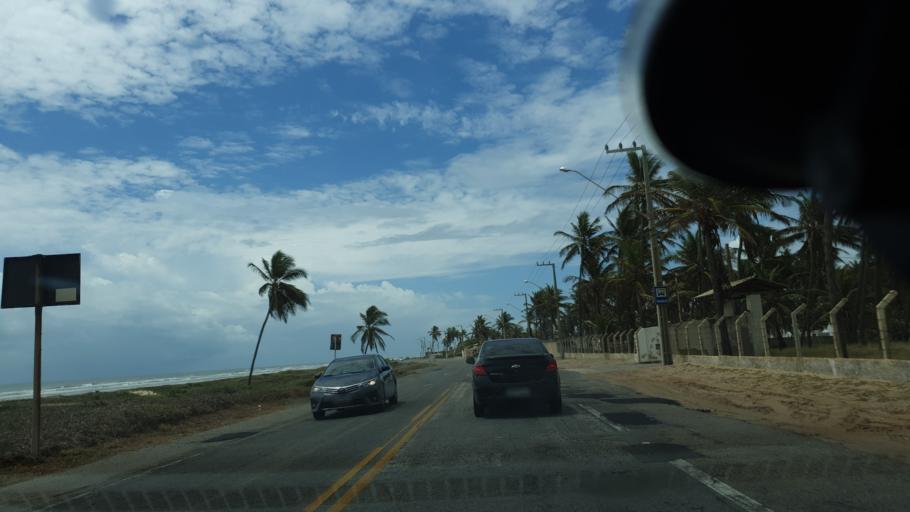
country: BR
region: Sergipe
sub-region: Sao Cristovao
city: Sao Cristovao
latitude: -11.0395
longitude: -37.0849
